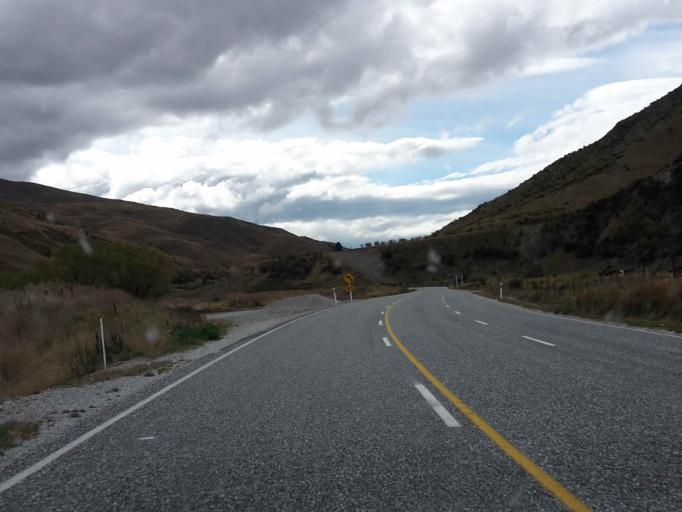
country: NZ
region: Otago
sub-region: Queenstown-Lakes District
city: Arrowtown
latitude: -44.9199
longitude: 168.9722
